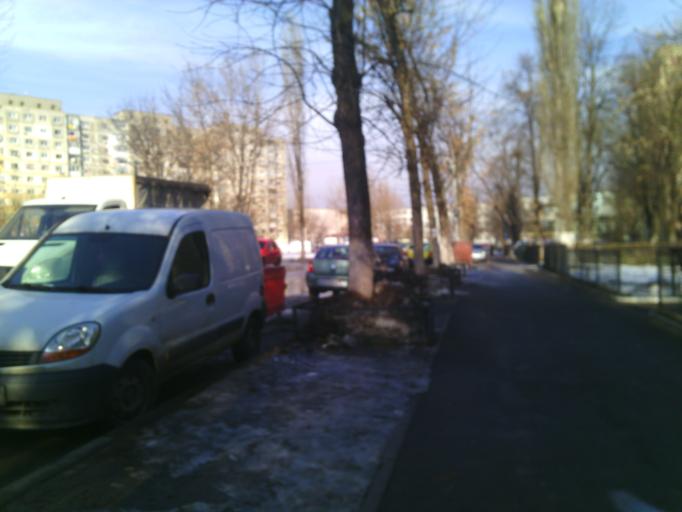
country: RO
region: Bucuresti
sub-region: Municipiul Bucuresti
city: Bucuresti
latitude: 44.3821
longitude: 26.1032
